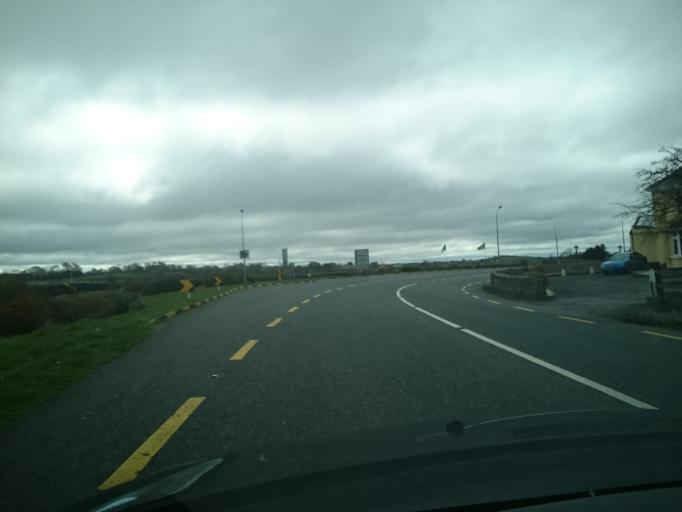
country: IE
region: Connaught
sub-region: Maigh Eo
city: Ballyhaunis
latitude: 53.7224
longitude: -8.8759
